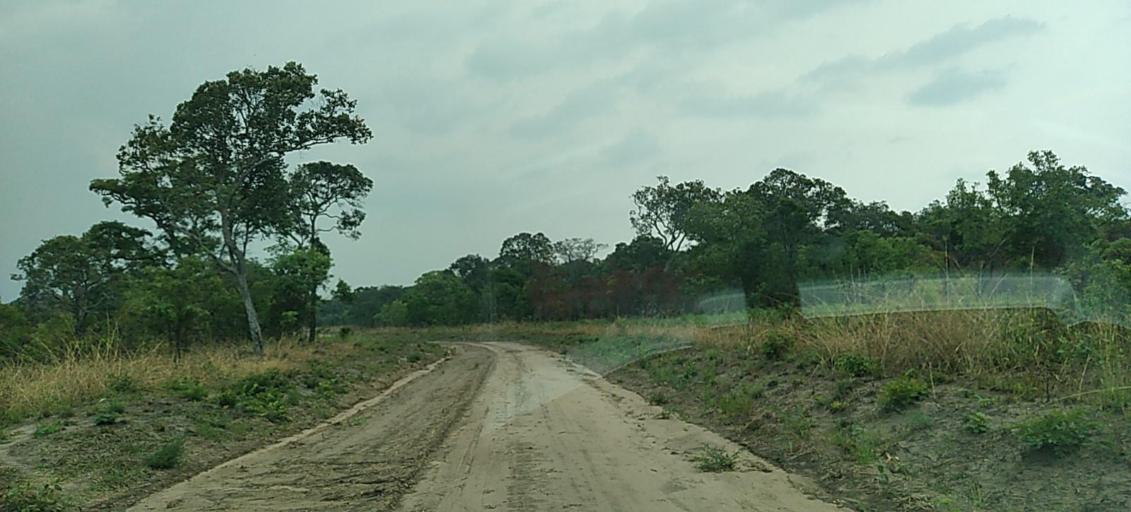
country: ZM
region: North-Western
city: Mwinilunga
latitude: -11.4222
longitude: 24.5949
